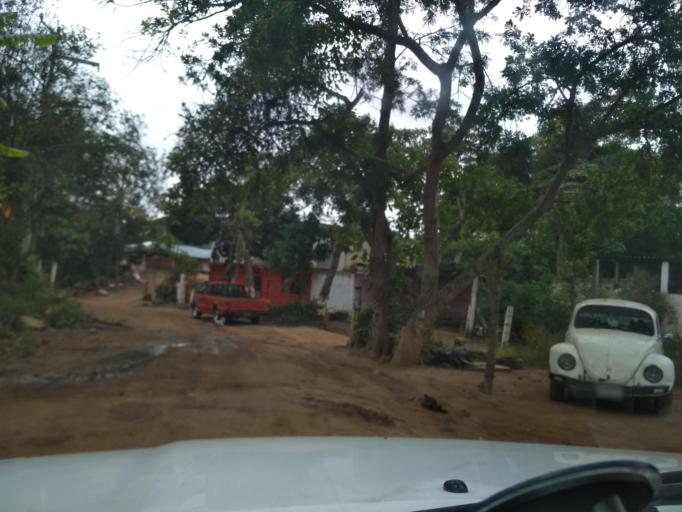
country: MX
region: Veracruz
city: El Castillo
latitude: 19.5435
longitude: -96.8479
